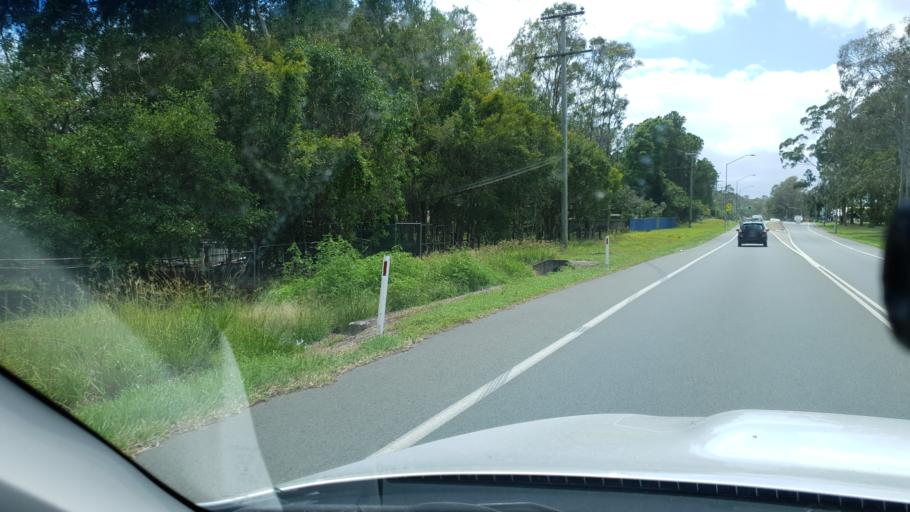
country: AU
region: Queensland
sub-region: Logan
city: Beenleigh
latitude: -27.6721
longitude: 153.2081
